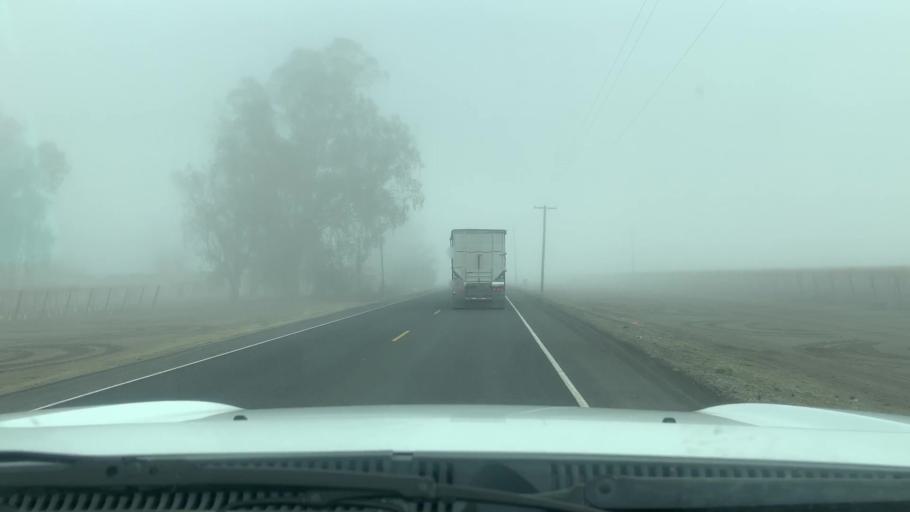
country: US
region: California
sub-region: Kern County
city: Buttonwillow
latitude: 35.4993
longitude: -119.5839
